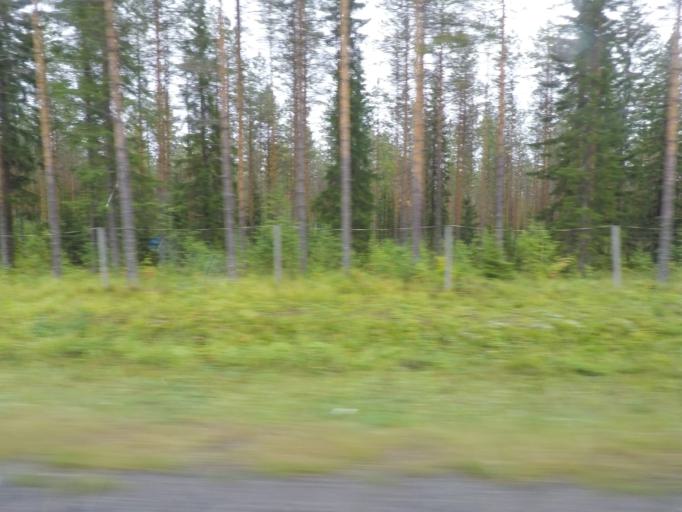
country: FI
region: Southern Savonia
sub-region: Pieksaemaeki
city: Juva
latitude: 61.9877
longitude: 27.8031
